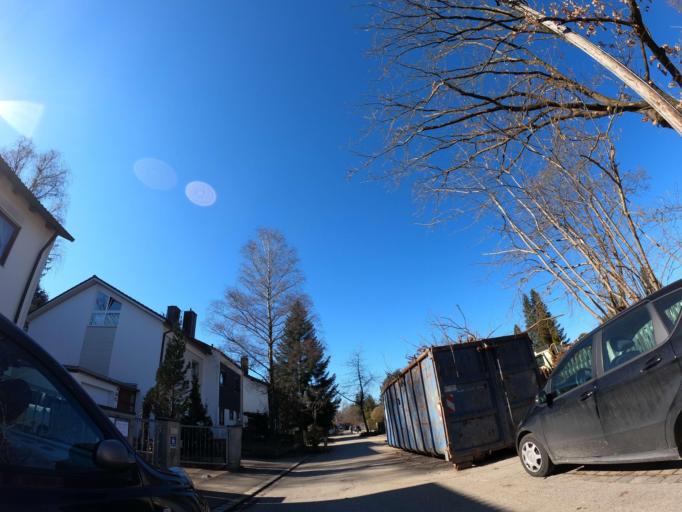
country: DE
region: Bavaria
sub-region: Upper Bavaria
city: Ottobrunn
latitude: 48.0762
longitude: 11.6762
